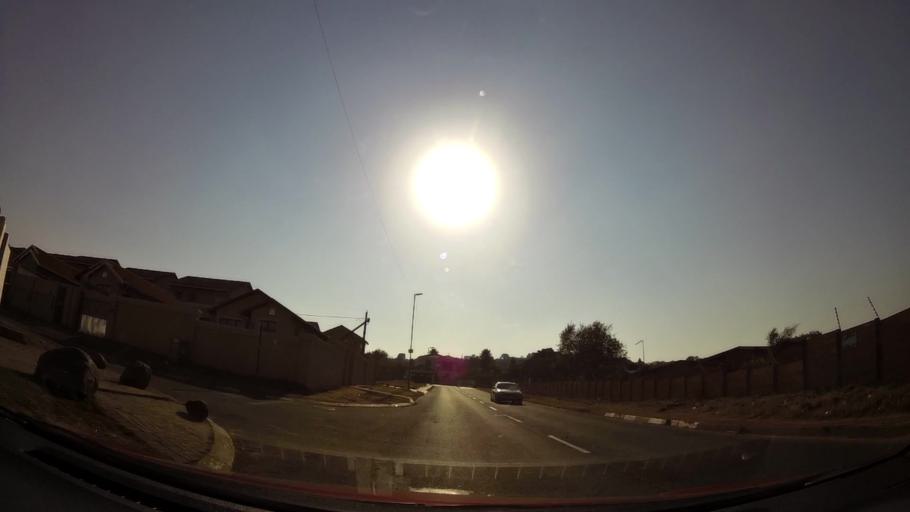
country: ZA
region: Gauteng
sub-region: City of Johannesburg Metropolitan Municipality
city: Soweto
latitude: -26.2909
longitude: 27.9520
